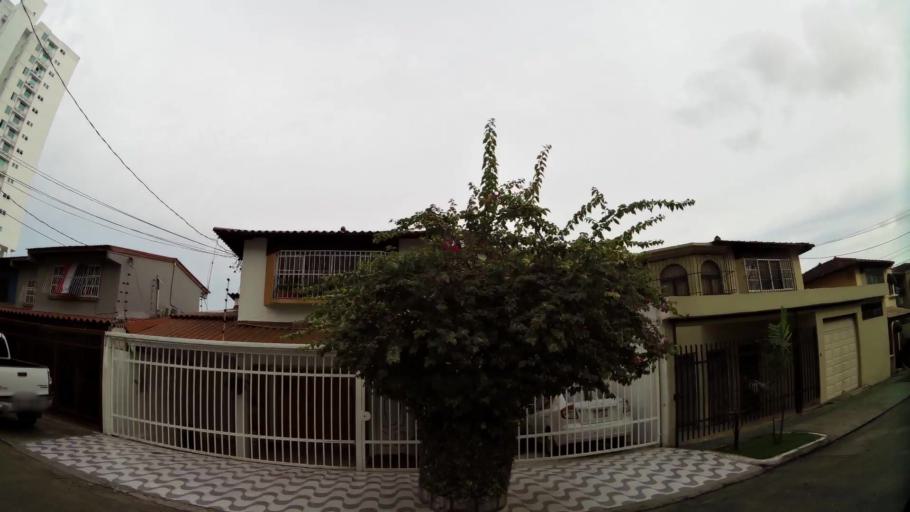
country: PA
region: Panama
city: Panama
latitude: 9.0095
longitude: -79.5120
